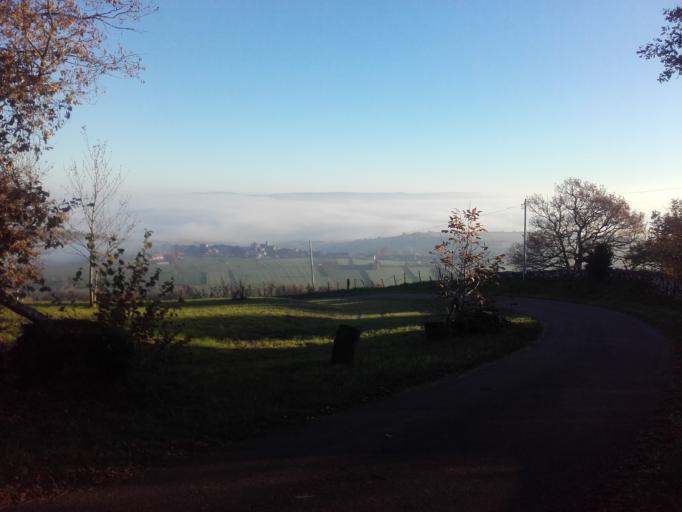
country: FR
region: Bourgogne
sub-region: Departement de la Cote-d'Or
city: Nolay
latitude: 46.9025
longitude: 4.6136
